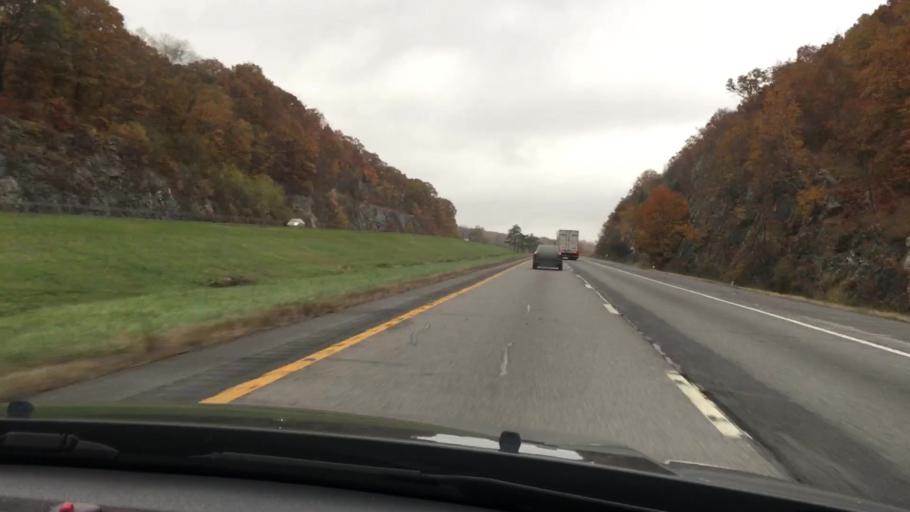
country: US
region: New York
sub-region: Putnam County
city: Lake Carmel
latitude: 41.4530
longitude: -73.6390
